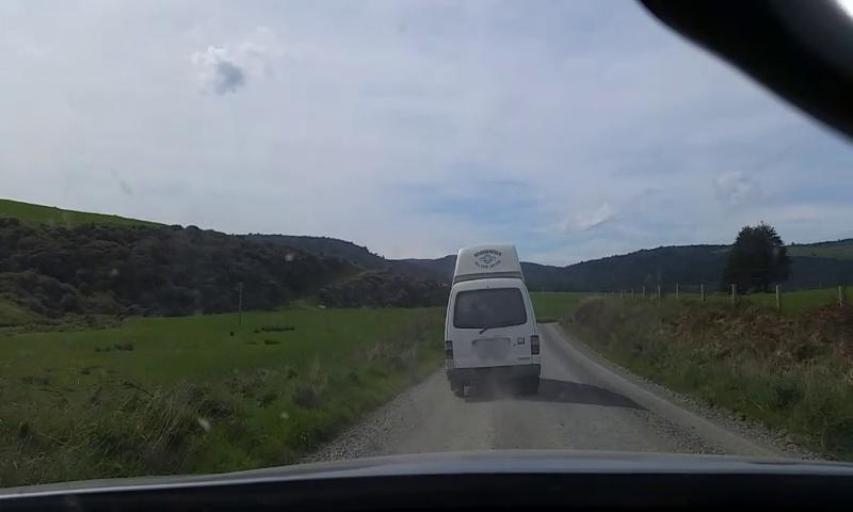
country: NZ
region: Otago
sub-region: Clutha District
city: Papatowai
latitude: -46.6275
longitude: 169.0046
